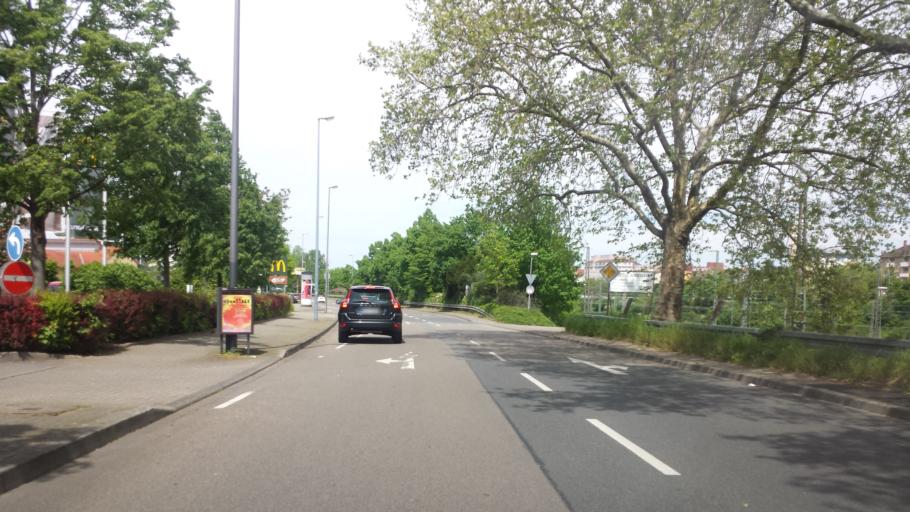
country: DE
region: Baden-Wuerttemberg
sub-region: Karlsruhe Region
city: Heidelberg
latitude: 49.3977
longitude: 8.6826
